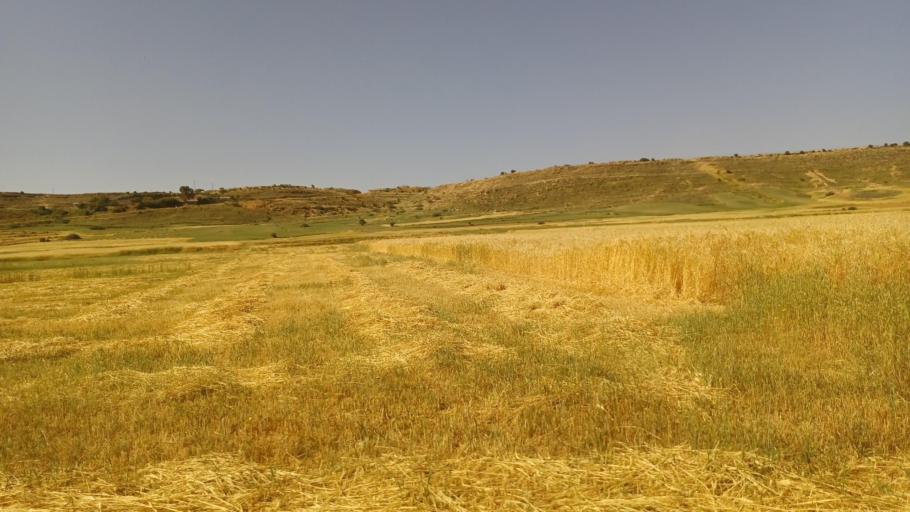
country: CY
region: Lefkosia
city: Mammari
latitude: 35.1704
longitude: 33.2308
